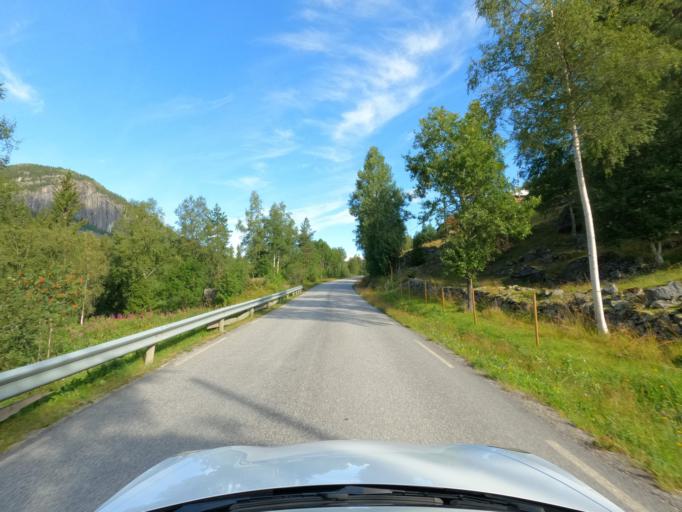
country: NO
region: Buskerud
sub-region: Nore og Uvdal
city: Rodberg
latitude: 60.0805
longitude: 8.7689
